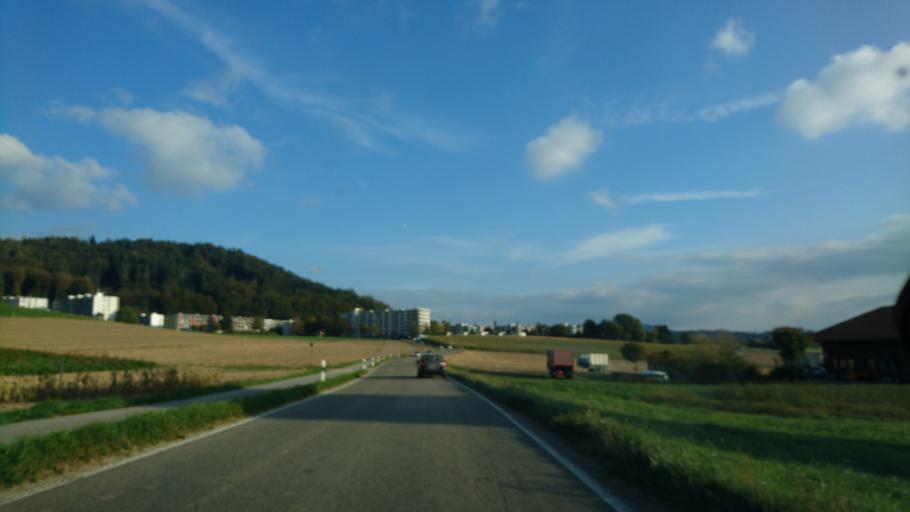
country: CH
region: Bern
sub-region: Bern-Mittelland District
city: Zollikofen
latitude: 46.9868
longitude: 7.4731
